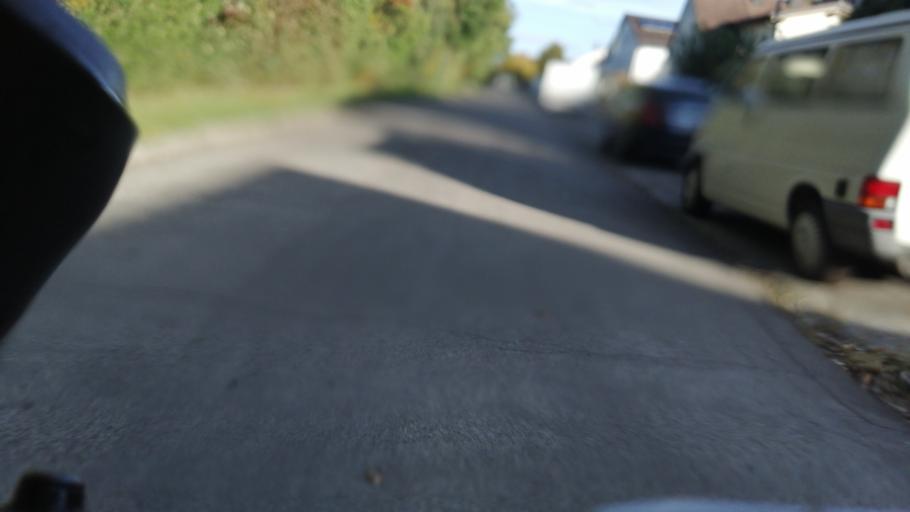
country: DE
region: Bavaria
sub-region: Upper Bavaria
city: Unterfoehring
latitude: 48.2091
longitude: 11.5979
